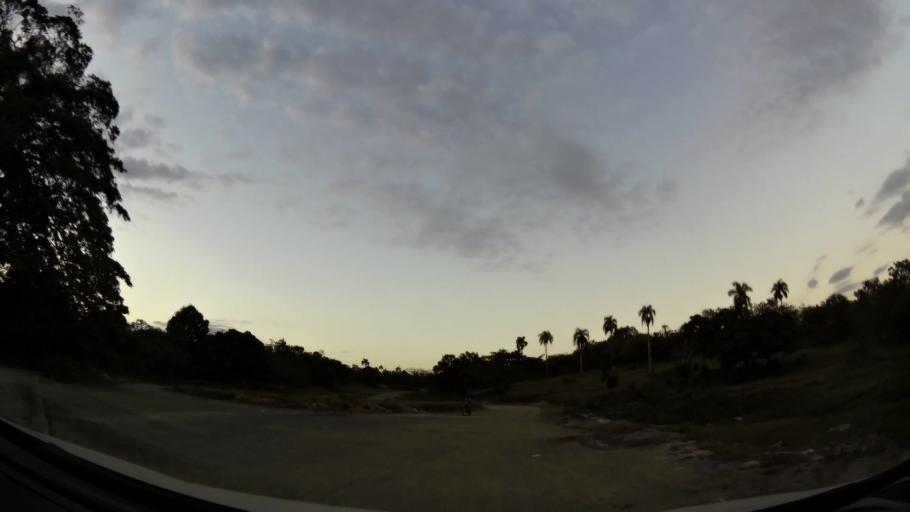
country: DO
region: Nacional
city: La Agustina
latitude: 18.5670
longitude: -69.9469
